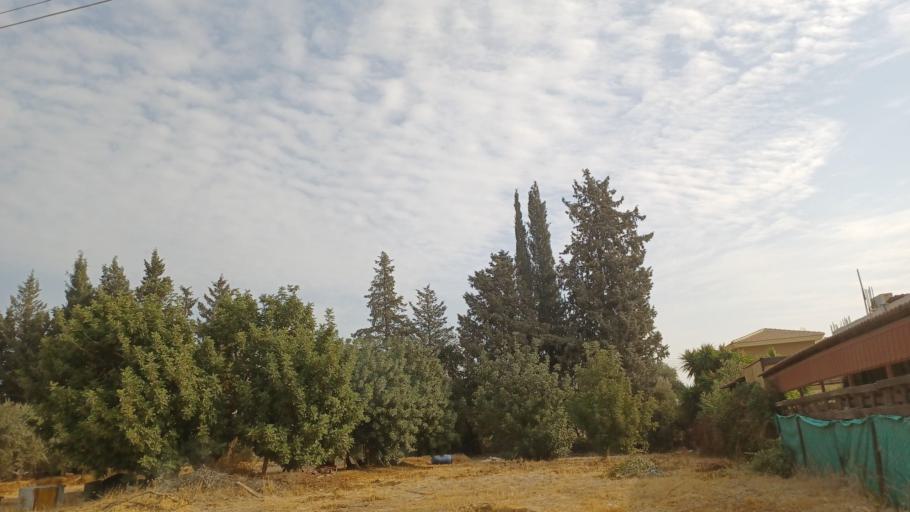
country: CY
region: Limassol
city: Ypsonas
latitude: 34.7000
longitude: 32.9566
